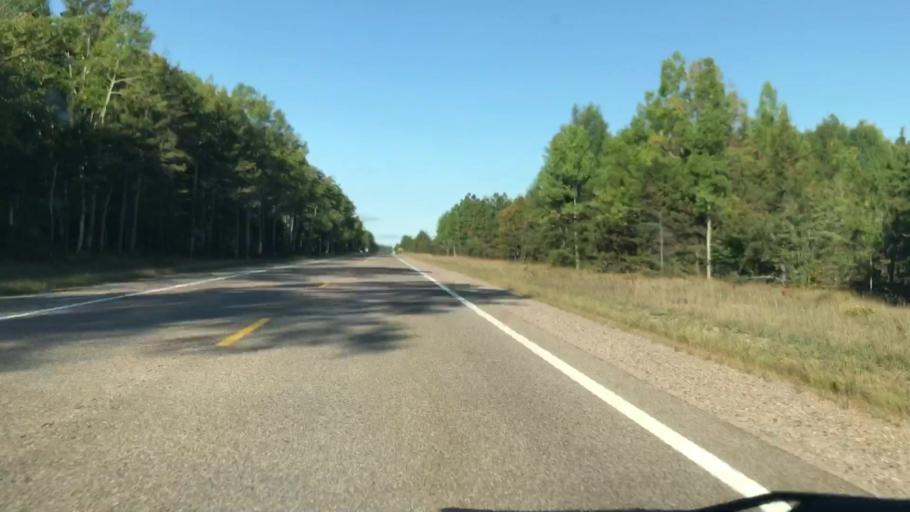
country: US
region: Michigan
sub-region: Mackinac County
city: Saint Ignace
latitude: 46.3584
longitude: -84.8550
